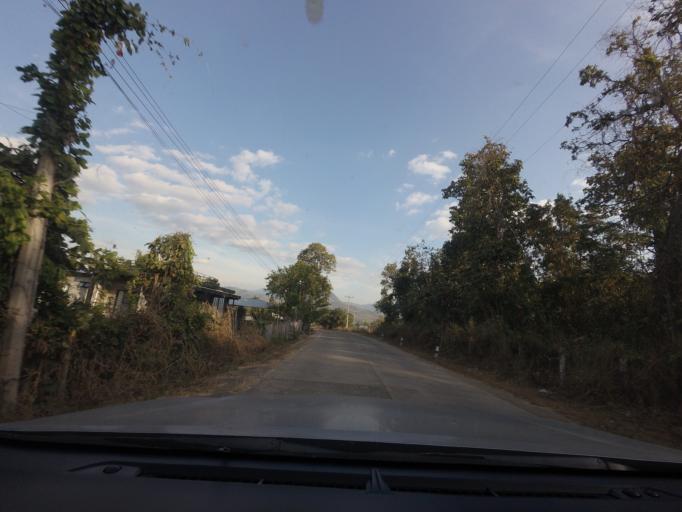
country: TH
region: Mae Hong Son
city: Wiang Nuea
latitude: 19.3852
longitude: 98.4240
